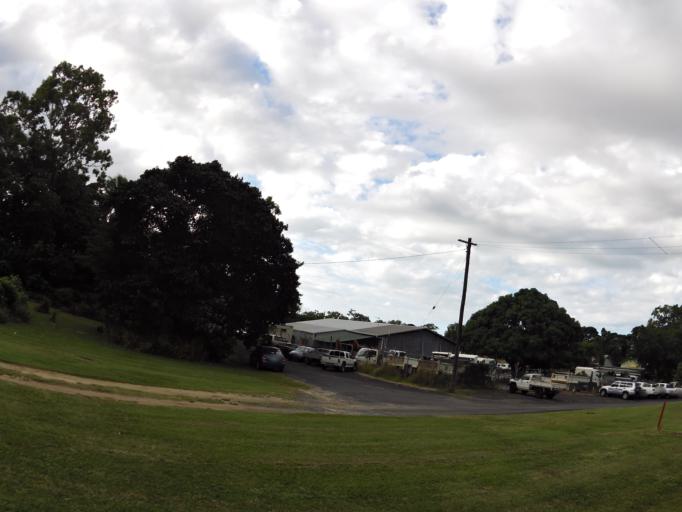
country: AU
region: Queensland
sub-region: Cairns
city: Redlynch
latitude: -16.8750
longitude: 145.7318
